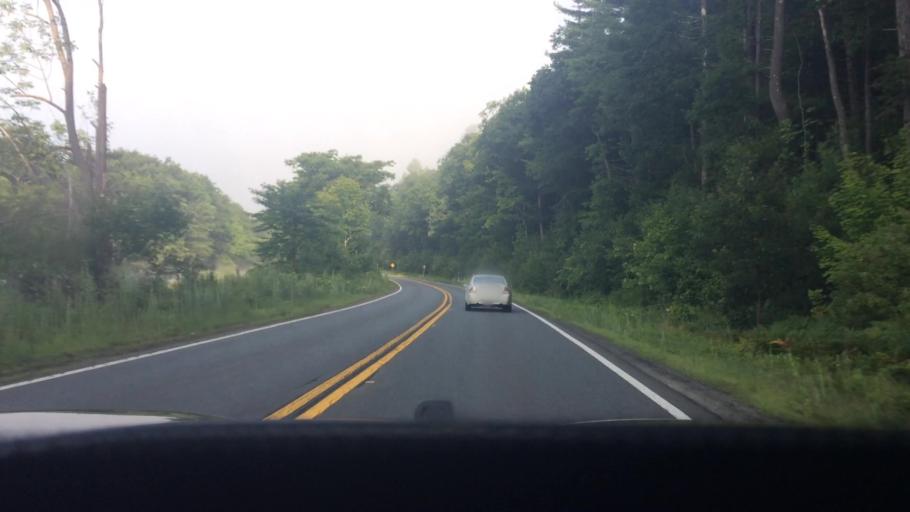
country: US
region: Massachusetts
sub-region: Franklin County
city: Erving
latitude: 42.6081
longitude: -72.4168
